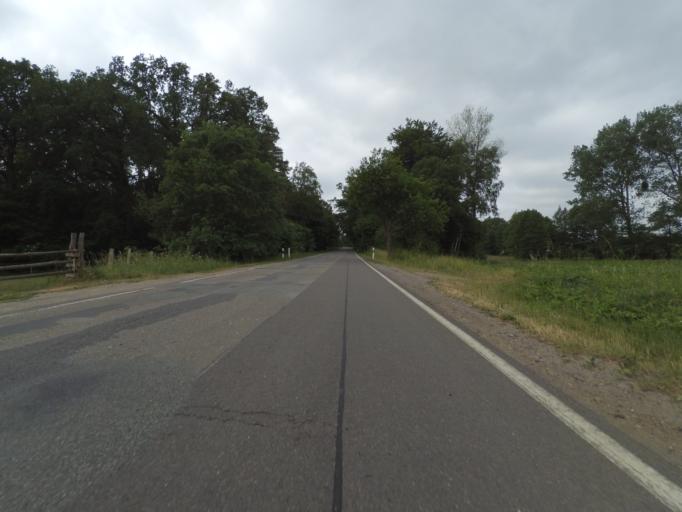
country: DE
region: Mecklenburg-Vorpommern
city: Krakow am See
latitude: 53.6265
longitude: 12.3416
